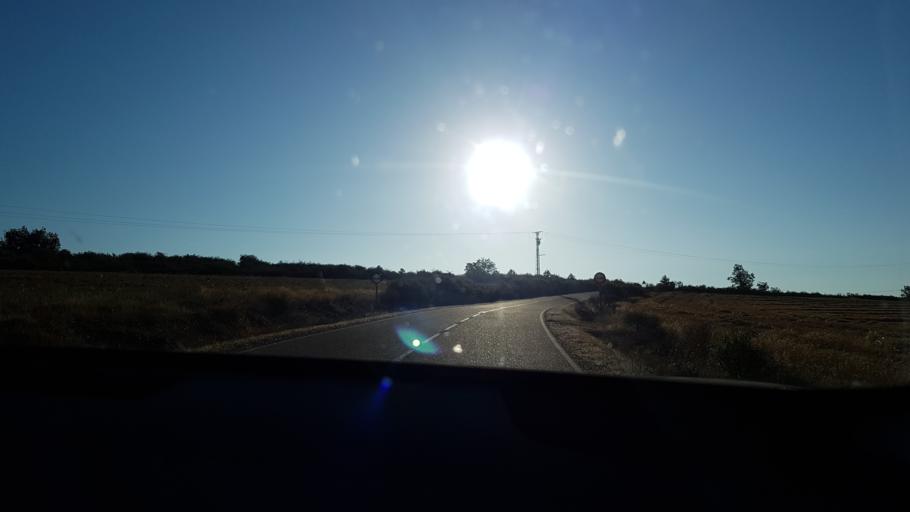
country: ES
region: Castille and Leon
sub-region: Provincia de Zamora
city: Samir de los Canos
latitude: 41.6636
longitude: -6.1816
